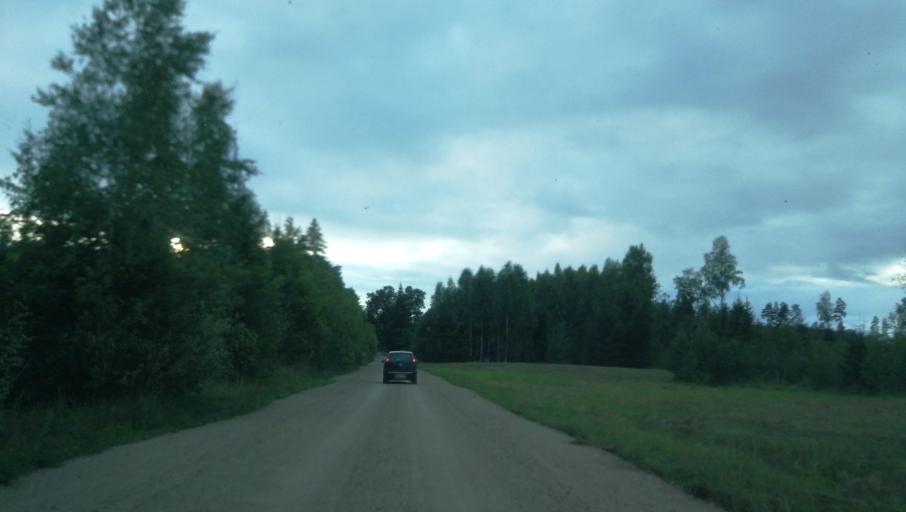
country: LV
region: Incukalns
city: Incukalns
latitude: 57.0294
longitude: 24.7916
